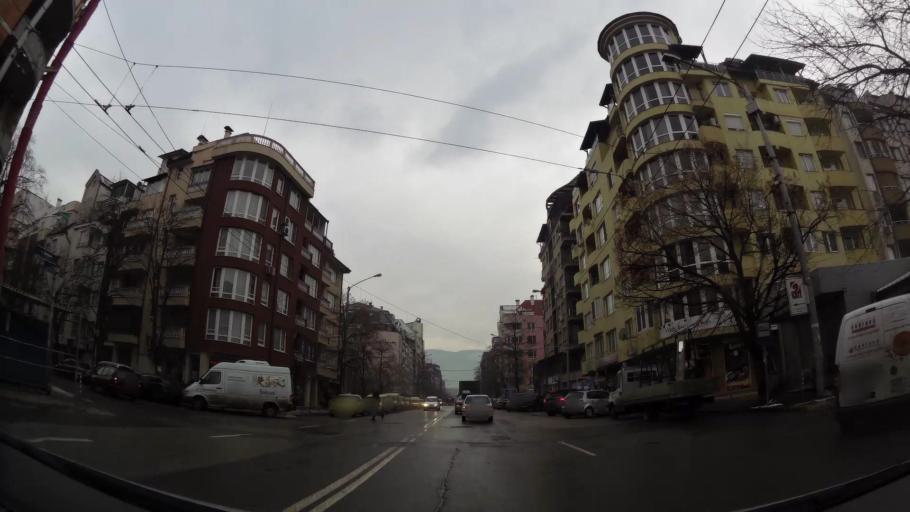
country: BG
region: Sofia-Capital
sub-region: Stolichna Obshtina
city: Sofia
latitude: 42.6786
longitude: 23.2911
